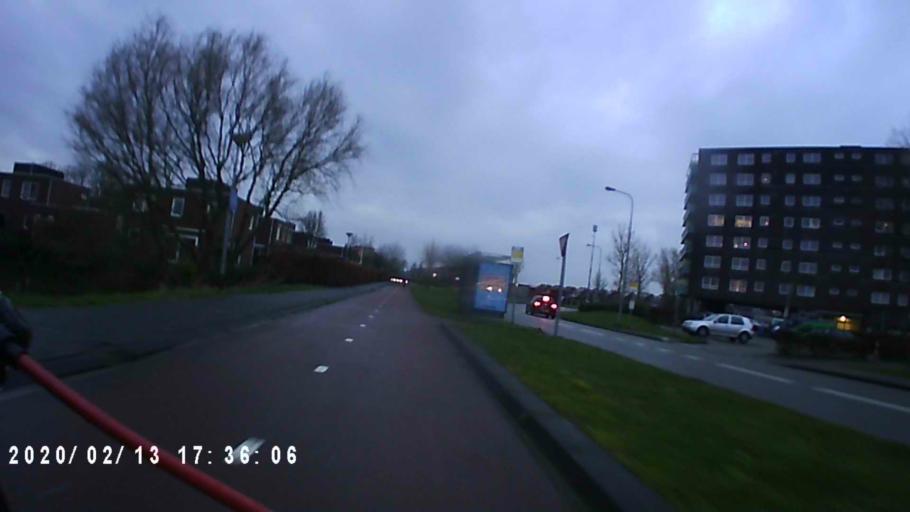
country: NL
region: Groningen
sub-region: Gemeente Groningen
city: Groningen
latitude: 53.2269
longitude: 6.5137
